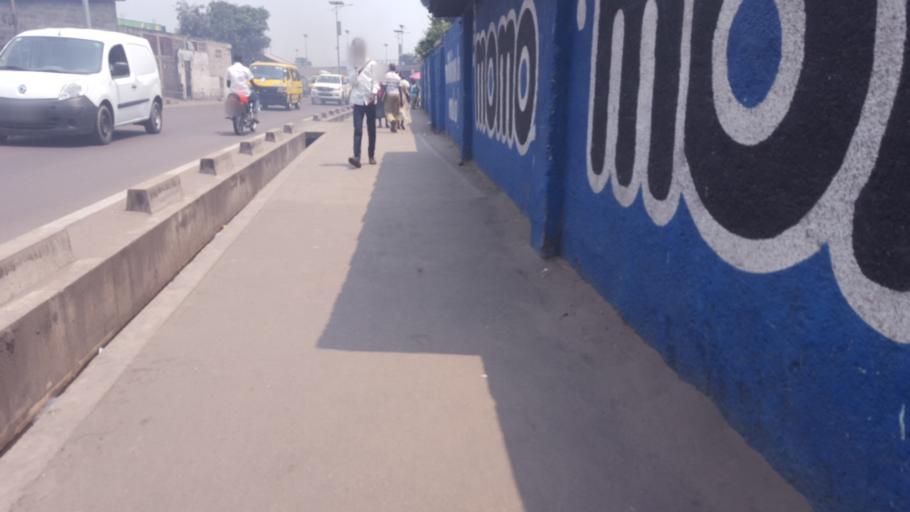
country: CD
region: Kinshasa
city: Masina
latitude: -4.3835
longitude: 15.3530
